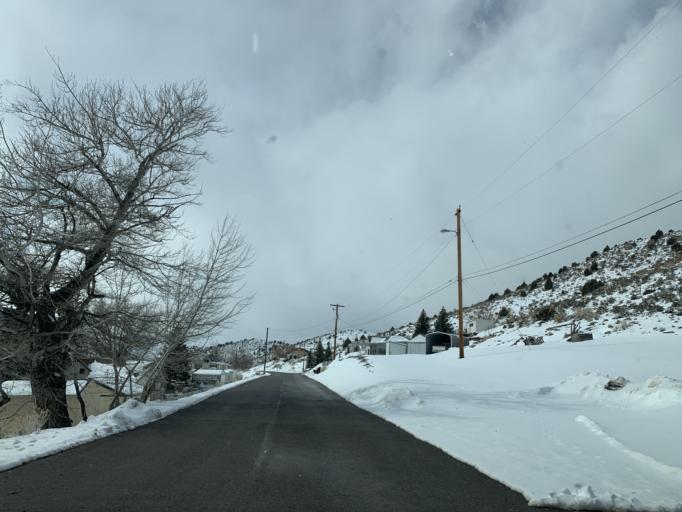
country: US
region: Utah
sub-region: Utah County
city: Genola
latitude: 39.9581
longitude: -112.1164
